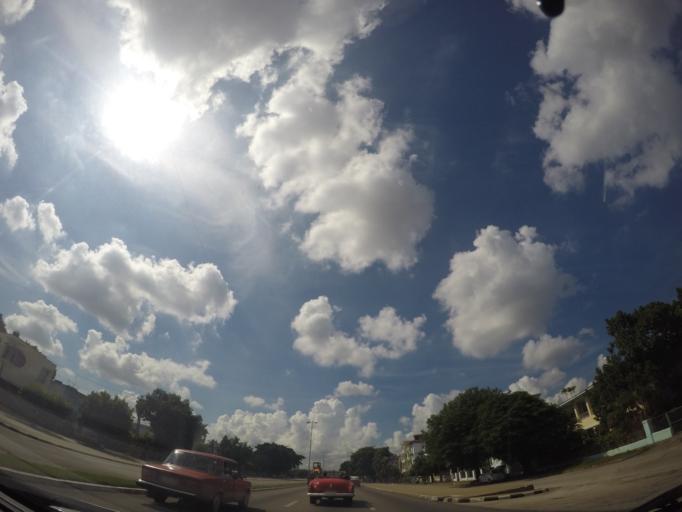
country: CU
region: La Habana
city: Havana
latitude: 23.1144
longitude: -82.4178
